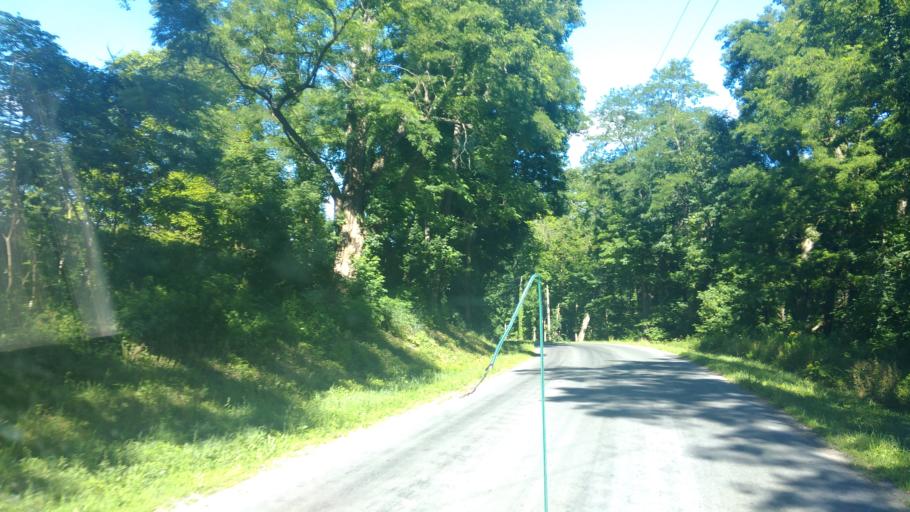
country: US
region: New York
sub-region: Wayne County
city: Clyde
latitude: 43.0233
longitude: -76.8481
